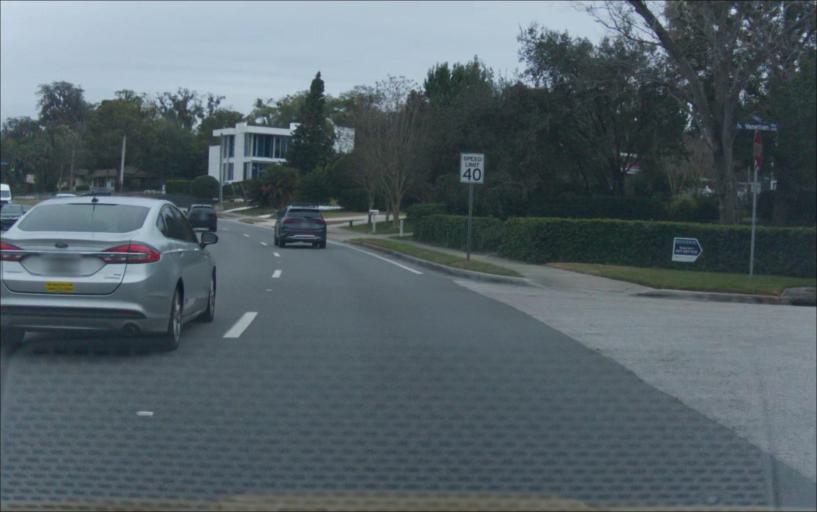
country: US
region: Florida
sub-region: Orange County
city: Winter Park
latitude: 28.6240
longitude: -81.3236
